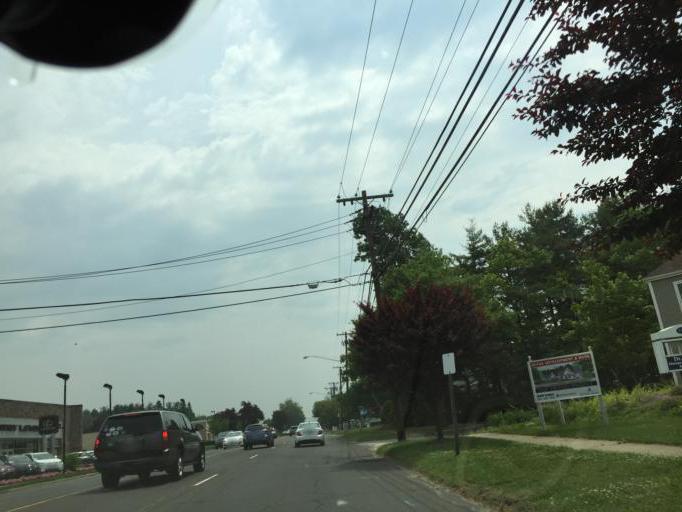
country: US
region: Connecticut
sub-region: Fairfield County
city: Southport
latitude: 41.1387
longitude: -73.3194
